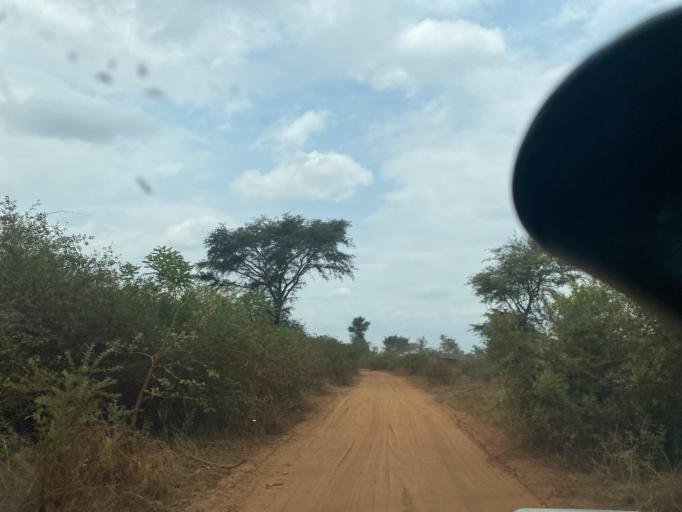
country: ZM
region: Lusaka
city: Chongwe
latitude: -15.4974
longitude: 28.8021
